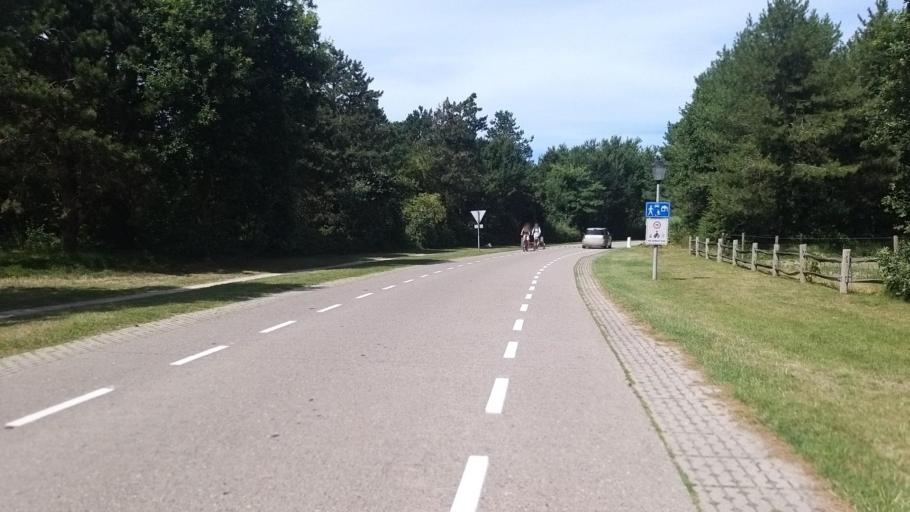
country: NL
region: North Holland
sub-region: Gemeente Texel
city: Den Burg
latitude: 53.1495
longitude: 4.8615
